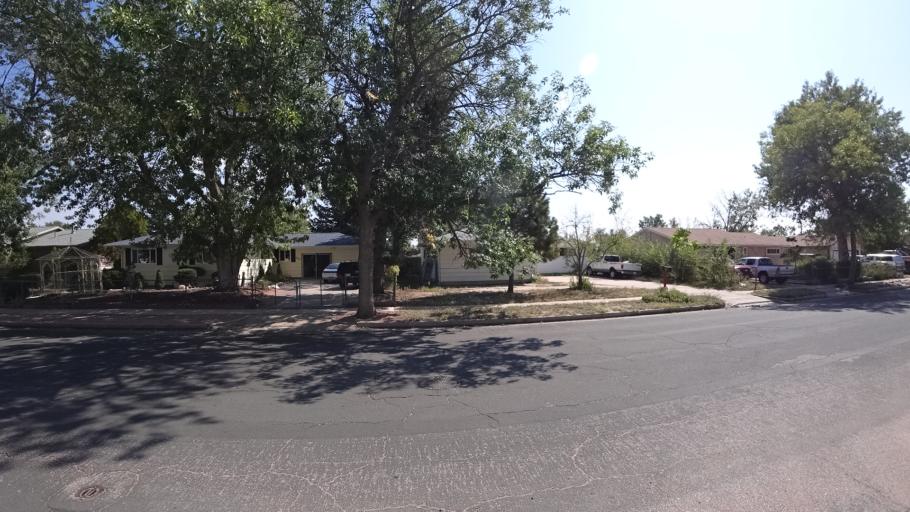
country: US
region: Colorado
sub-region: El Paso County
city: Colorado Springs
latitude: 38.8220
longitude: -104.7836
